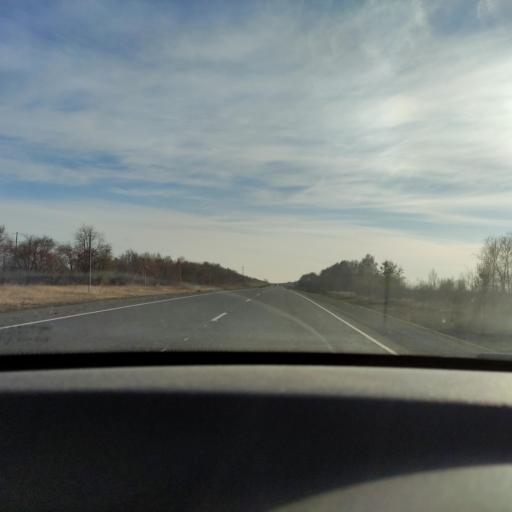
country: RU
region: Samara
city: Krasnoarmeyskoye
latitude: 52.8168
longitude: 50.0102
